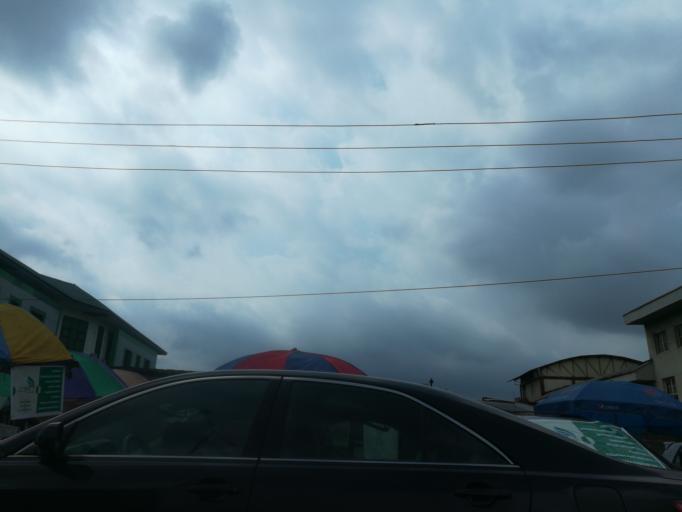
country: NG
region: Lagos
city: Ikeja
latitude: 6.6251
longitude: 3.3609
